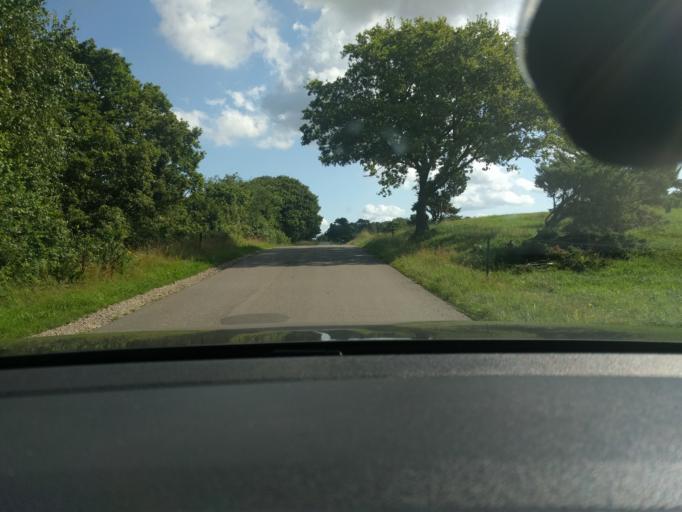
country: DK
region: Central Jutland
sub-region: Viborg Kommune
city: Stoholm
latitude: 56.4885
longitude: 9.2732
